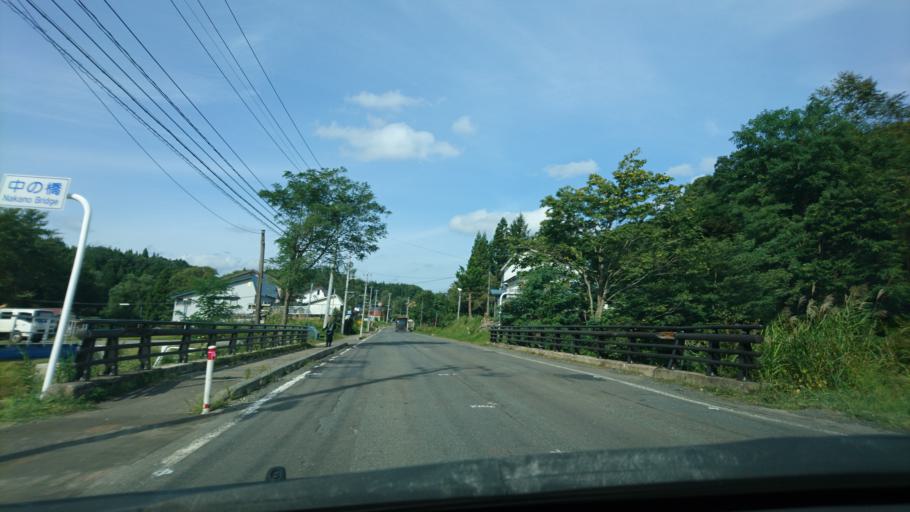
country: JP
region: Akita
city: Yokotemachi
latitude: 39.2982
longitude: 140.7350
